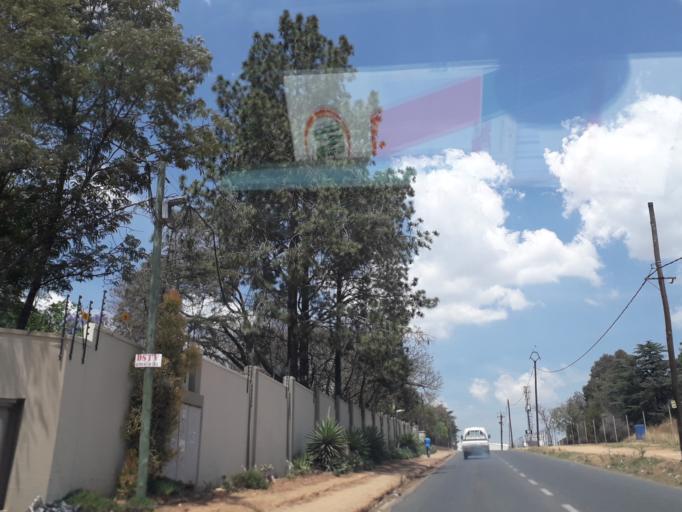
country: ZA
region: Gauteng
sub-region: West Rand District Municipality
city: Muldersdriseloop
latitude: -26.0692
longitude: 27.9238
